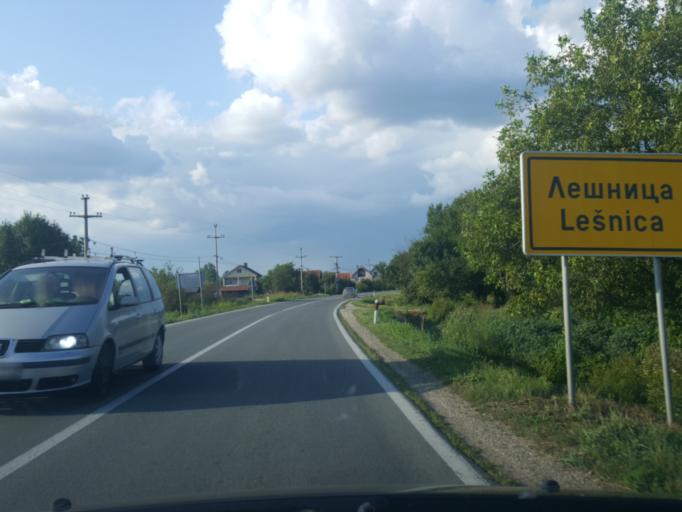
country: RS
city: Lesnica
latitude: 44.6330
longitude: 19.2740
